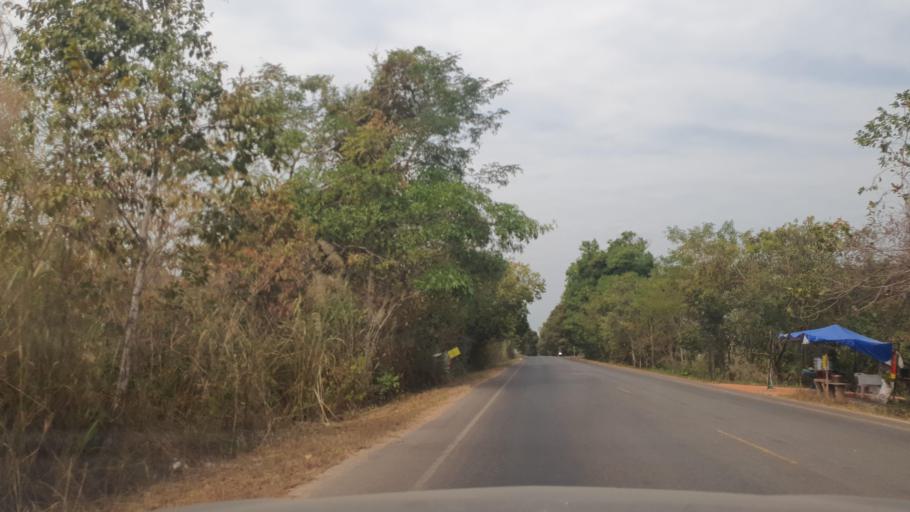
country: TH
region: Changwat Bueng Kan
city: Bung Khla
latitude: 18.2247
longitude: 104.0347
